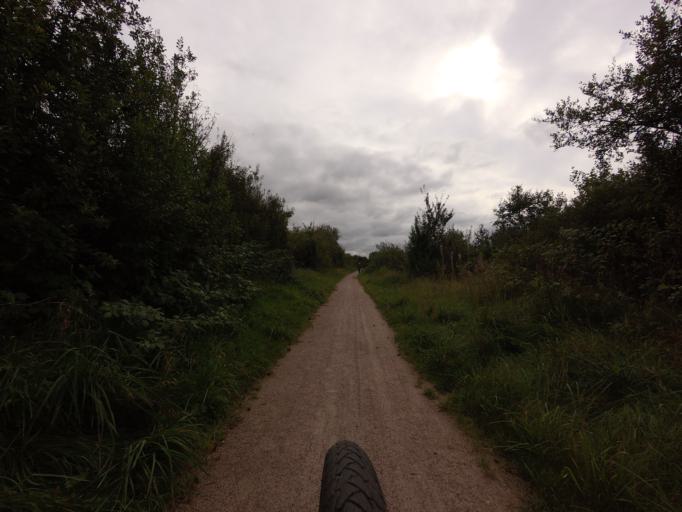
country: DK
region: South Denmark
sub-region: Billund Kommune
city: Billund
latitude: 55.8209
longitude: 9.0317
